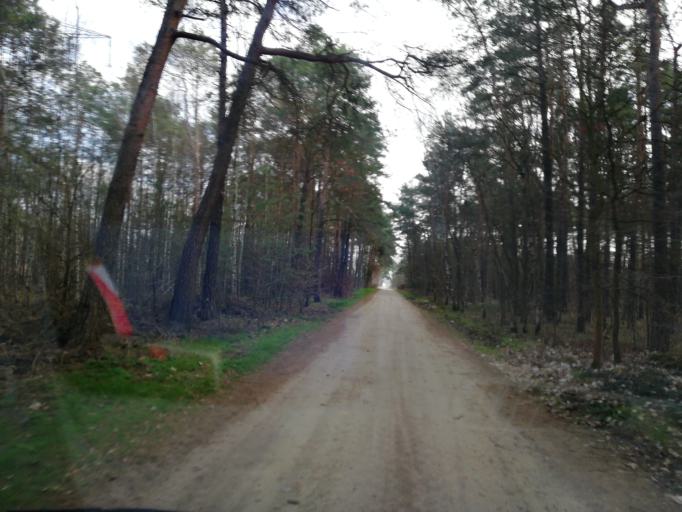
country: DE
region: Brandenburg
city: Finsterwalde
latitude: 51.6583
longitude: 13.6954
